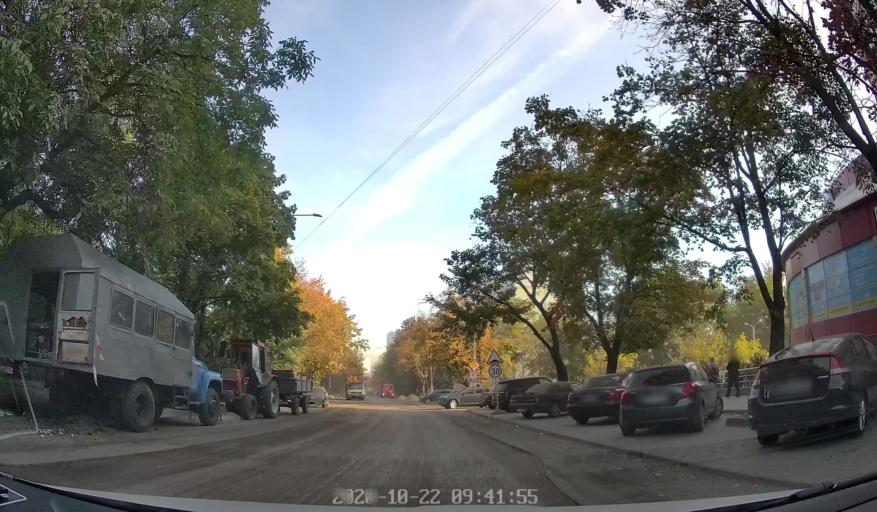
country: MD
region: Chisinau
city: Chisinau
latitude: 46.9978
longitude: 28.8350
